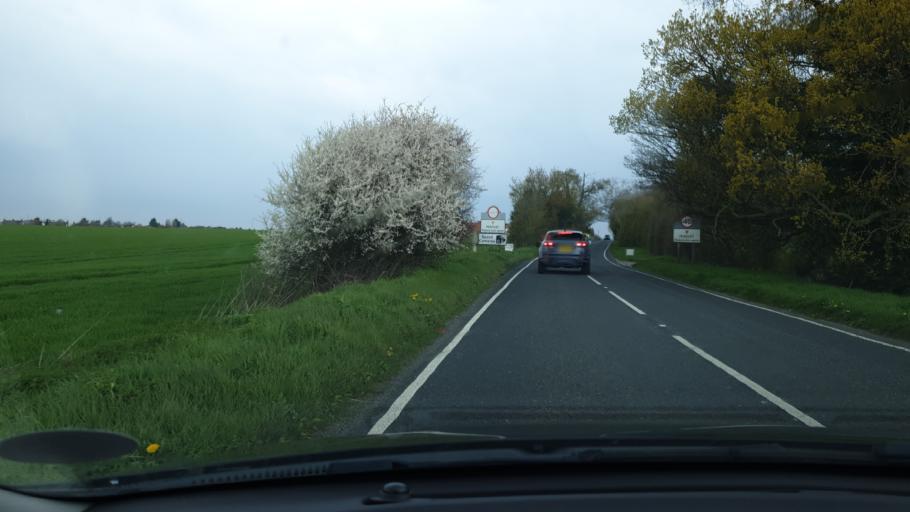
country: GB
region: England
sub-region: Essex
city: Manningtree
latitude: 51.9363
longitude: 1.0625
